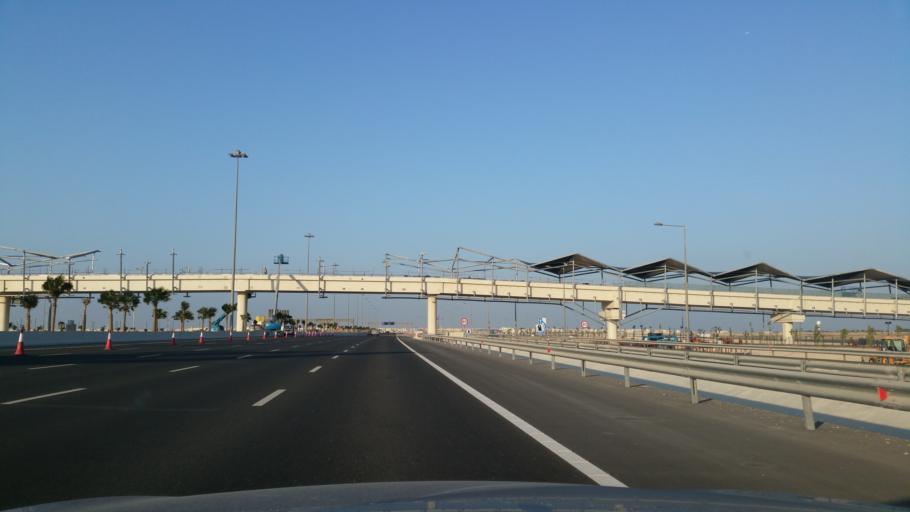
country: QA
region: Al Khawr
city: Al Khawr
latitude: 25.6469
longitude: 51.4953
